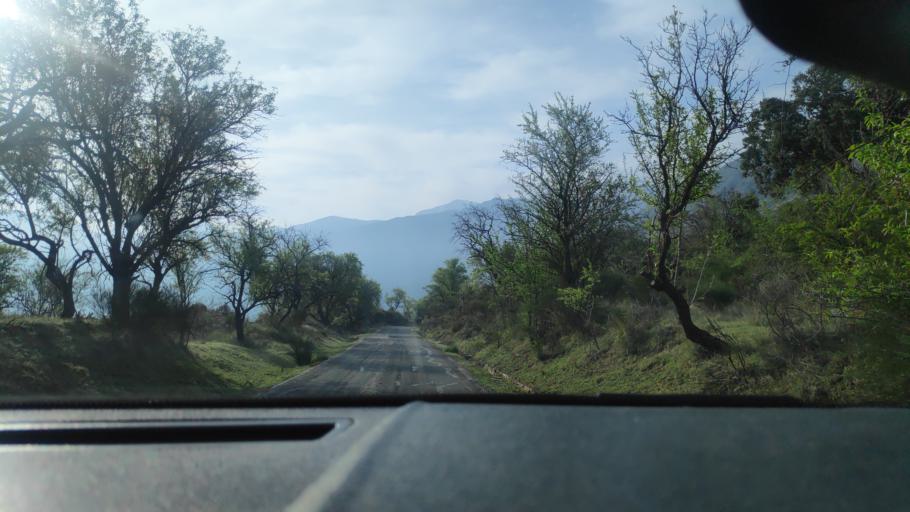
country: ES
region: Andalusia
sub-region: Provincia de Jaen
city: Torres
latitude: 37.7854
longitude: -3.4813
